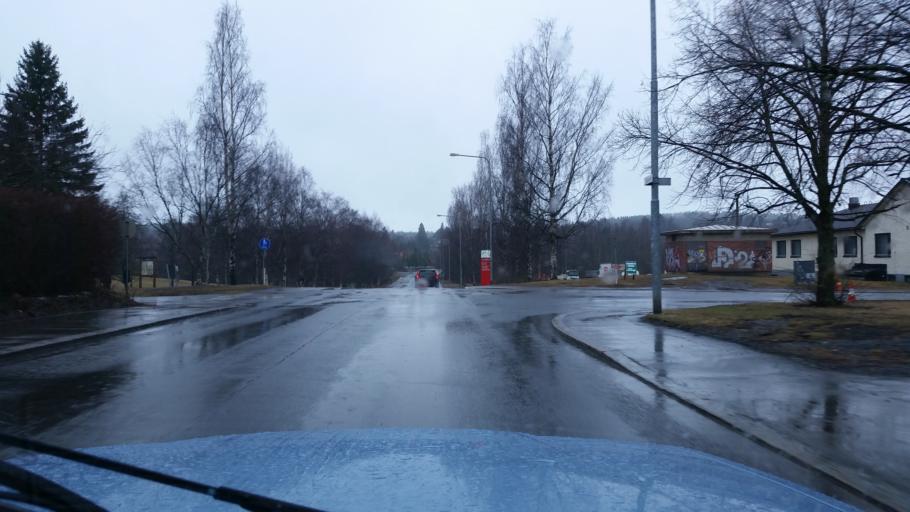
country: FI
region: Pirkanmaa
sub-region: Tampere
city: Tampere
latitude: 61.4764
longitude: 23.7980
